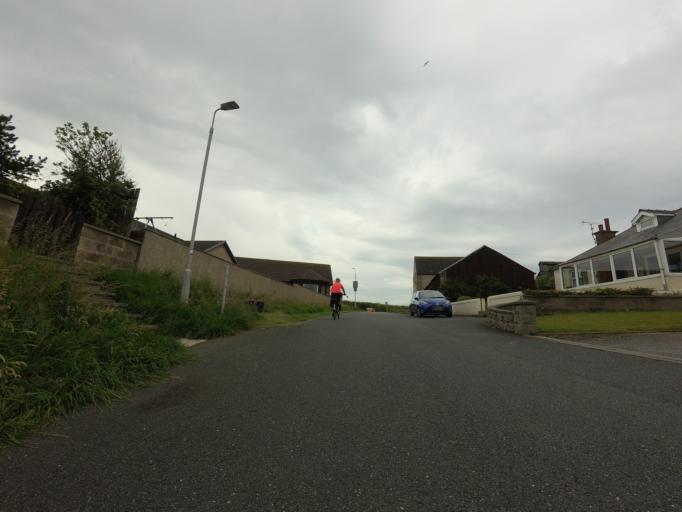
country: GB
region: Scotland
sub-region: Aberdeenshire
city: Whitehills
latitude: 57.6776
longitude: -2.5863
